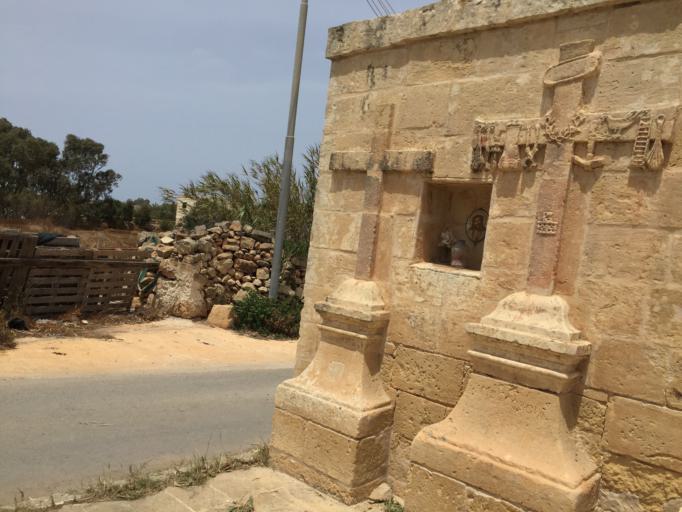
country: MT
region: Marsaskala
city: Marsaskala
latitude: 35.8691
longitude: 14.5549
